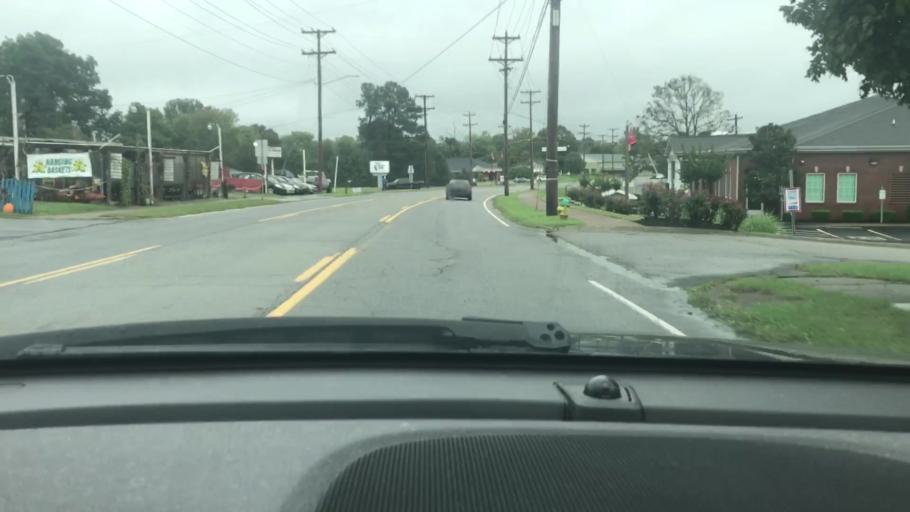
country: US
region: Tennessee
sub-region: Dickson County
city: White Bluff
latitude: 36.1084
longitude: -87.2255
